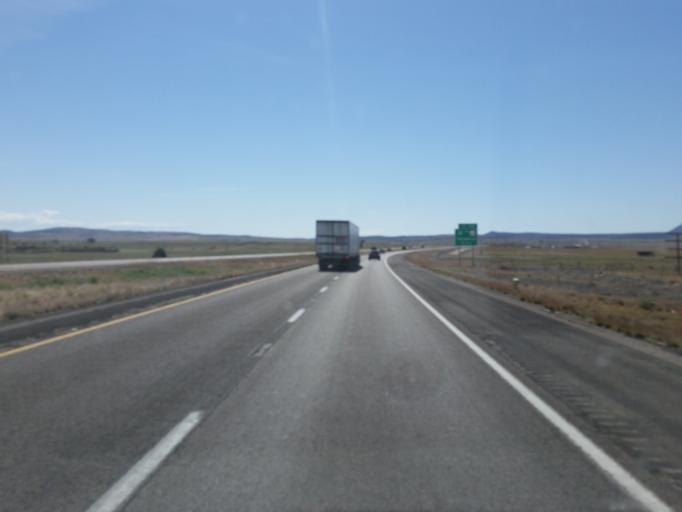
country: US
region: Arizona
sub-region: Yavapai County
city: Paulden
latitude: 35.3154
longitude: -112.8689
